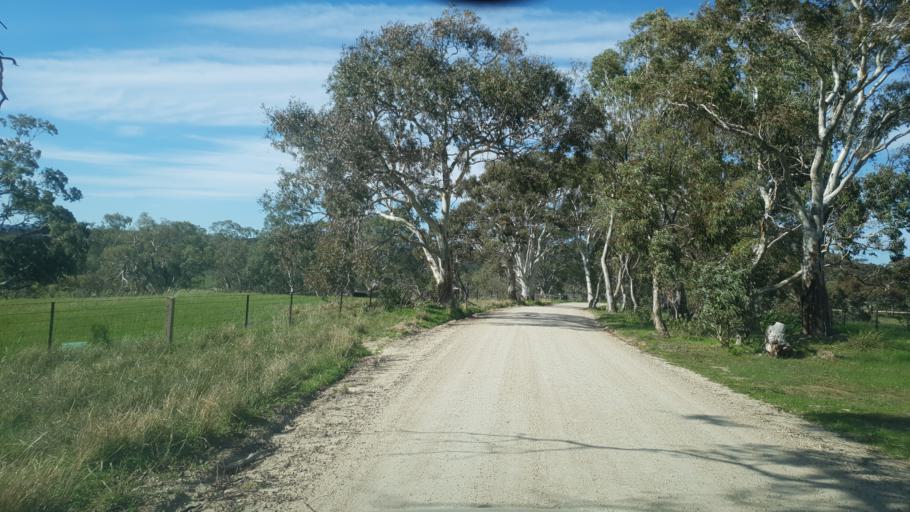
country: AU
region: South Australia
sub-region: Playford
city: One Tree Hill
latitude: -34.6413
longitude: 138.8139
